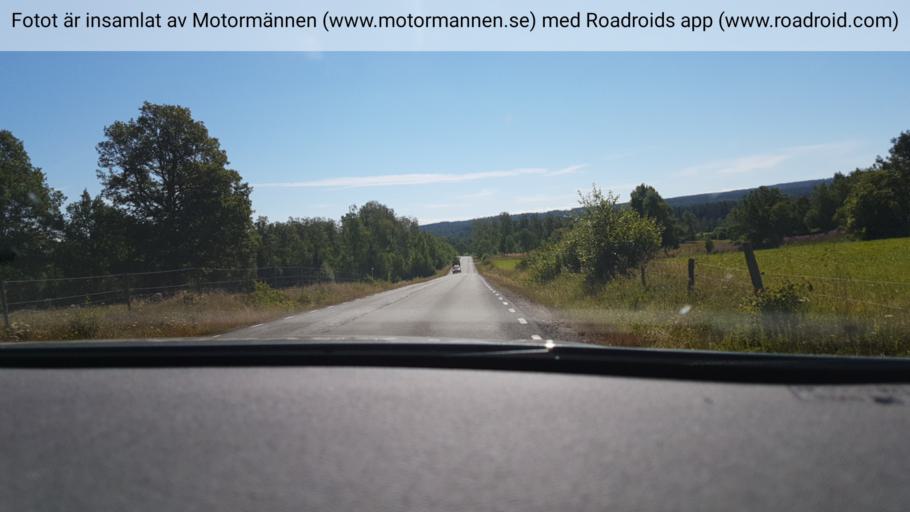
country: SE
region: Vaestra Goetaland
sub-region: Tidaholms Kommun
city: Tidaholm
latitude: 58.1428
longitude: 13.9926
